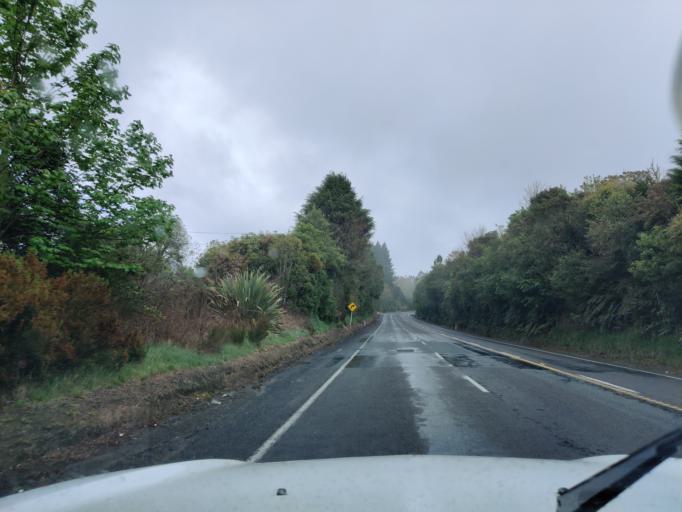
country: NZ
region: Bay of Plenty
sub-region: Rotorua District
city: Rotorua
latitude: -38.0744
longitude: 176.1660
